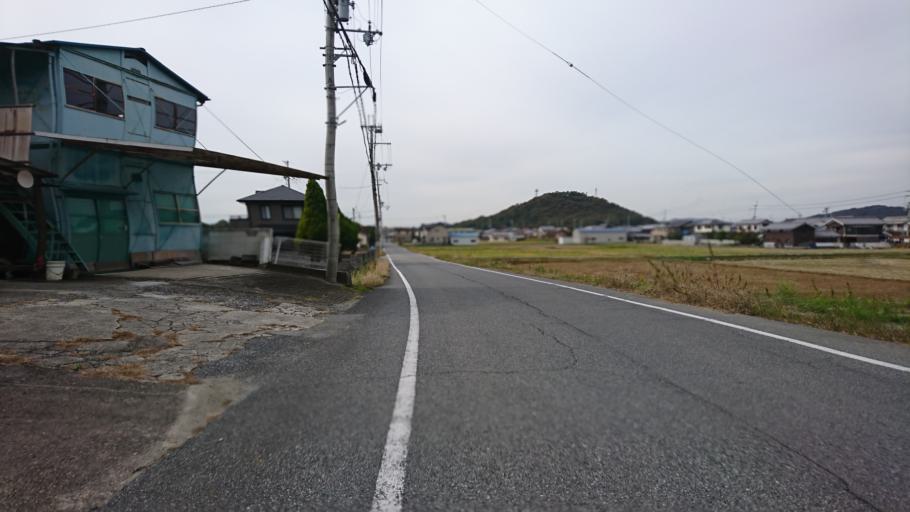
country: JP
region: Hyogo
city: Kakogawacho-honmachi
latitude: 34.7869
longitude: 134.8978
